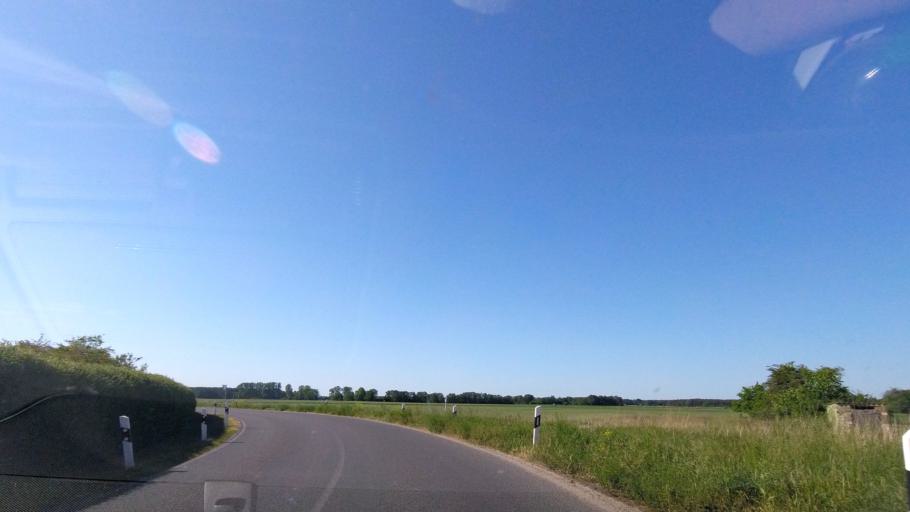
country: DE
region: Brandenburg
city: Brandenburg an der Havel
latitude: 52.3765
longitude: 12.6377
